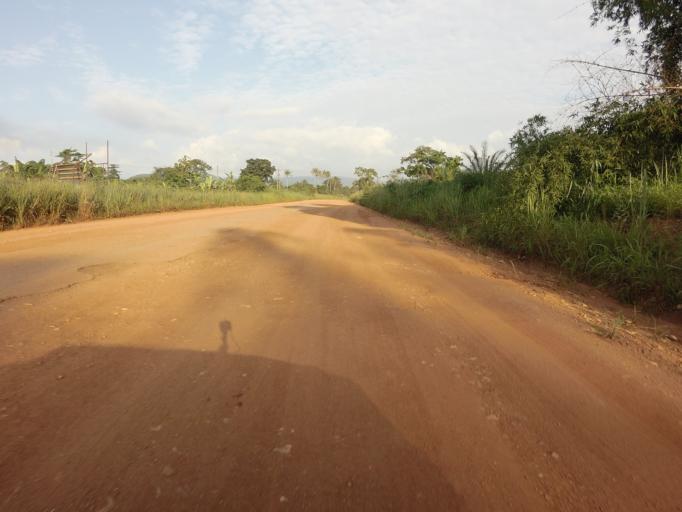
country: GH
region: Volta
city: Kpandu
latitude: 6.9867
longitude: 0.4446
